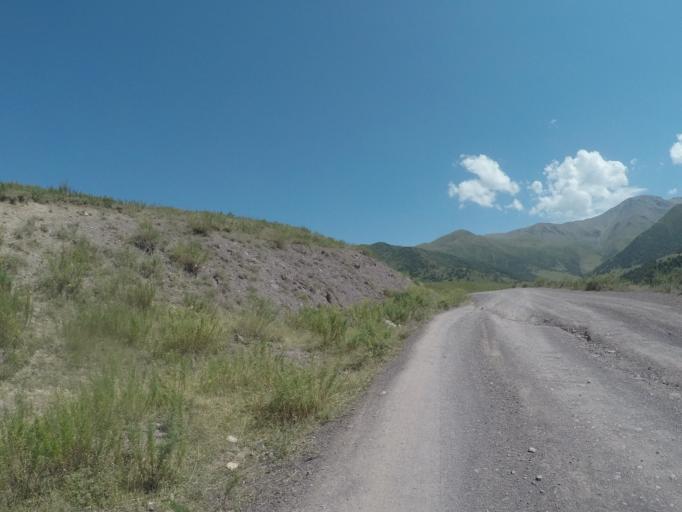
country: KG
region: Chuy
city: Bishkek
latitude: 42.6473
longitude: 74.5226
